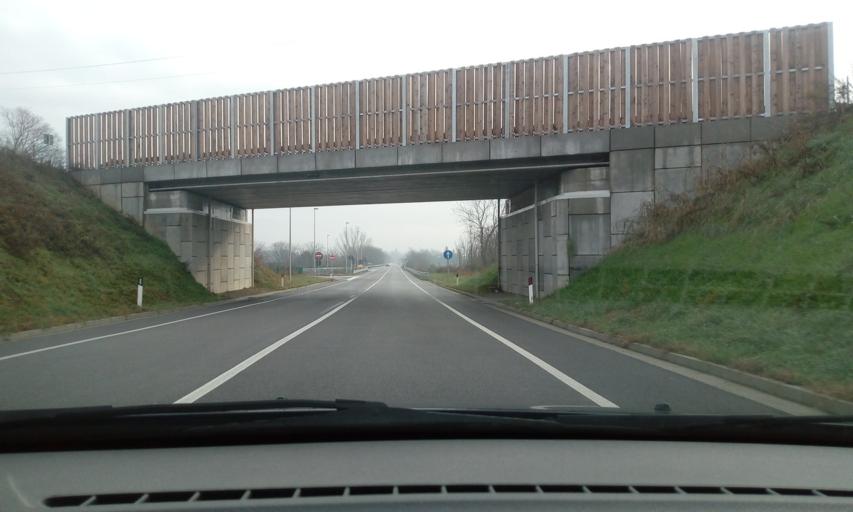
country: IT
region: Friuli Venezia Giulia
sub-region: Provincia di Gorizia
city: Savogna d'Isonzo
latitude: 45.9235
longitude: 13.5660
